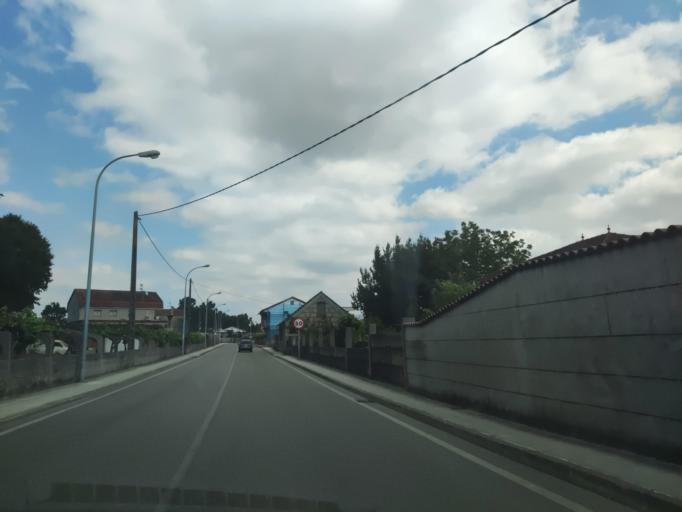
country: ES
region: Galicia
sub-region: Provincia de Pontevedra
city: Porrino
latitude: 42.1570
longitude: -8.6285
